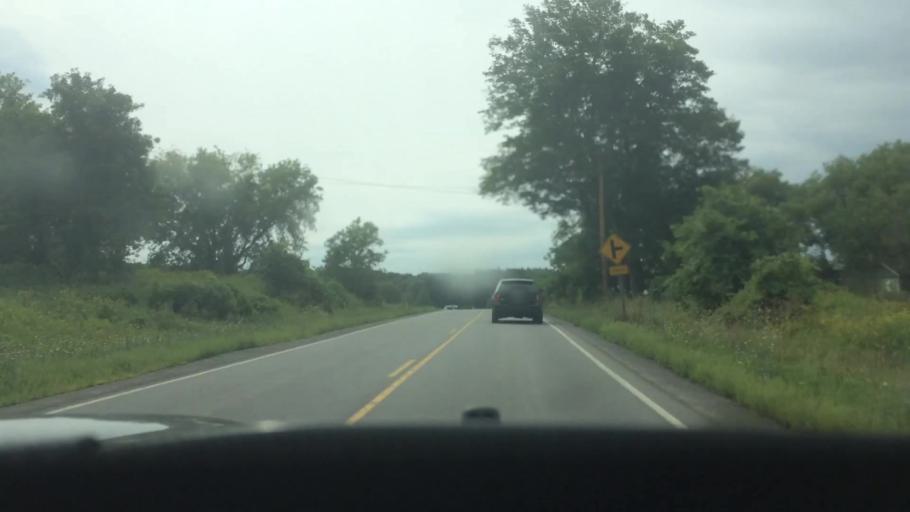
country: US
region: New York
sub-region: St. Lawrence County
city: Canton
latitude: 44.4741
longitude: -75.2394
